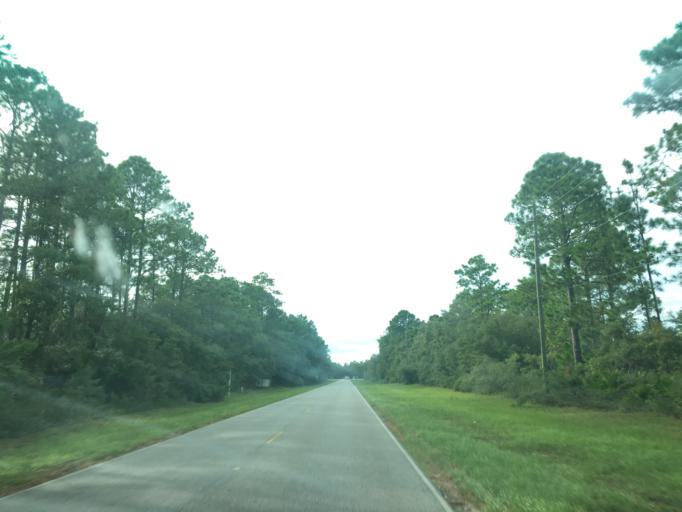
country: US
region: Florida
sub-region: Wakulla County
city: Crawfordville
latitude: 29.9402
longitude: -84.3837
